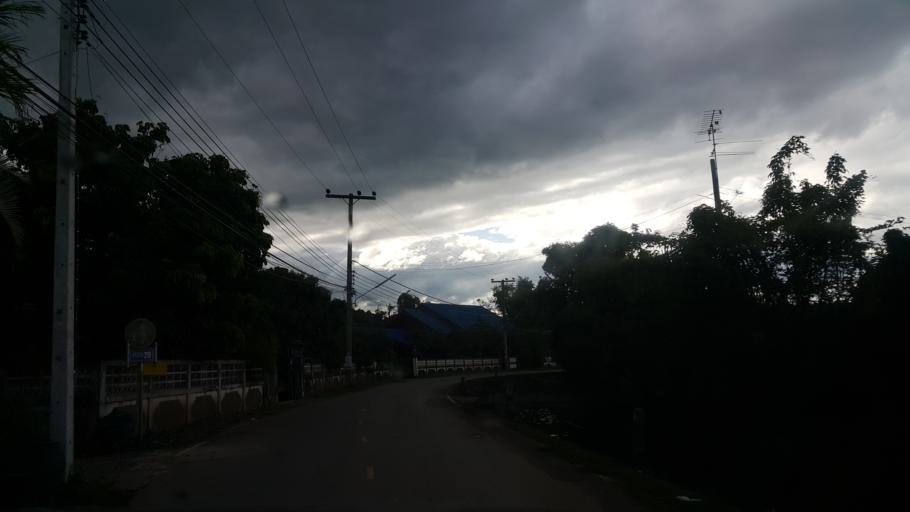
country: TH
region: Chiang Mai
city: Mae Taeng
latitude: 19.0792
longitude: 98.9516
